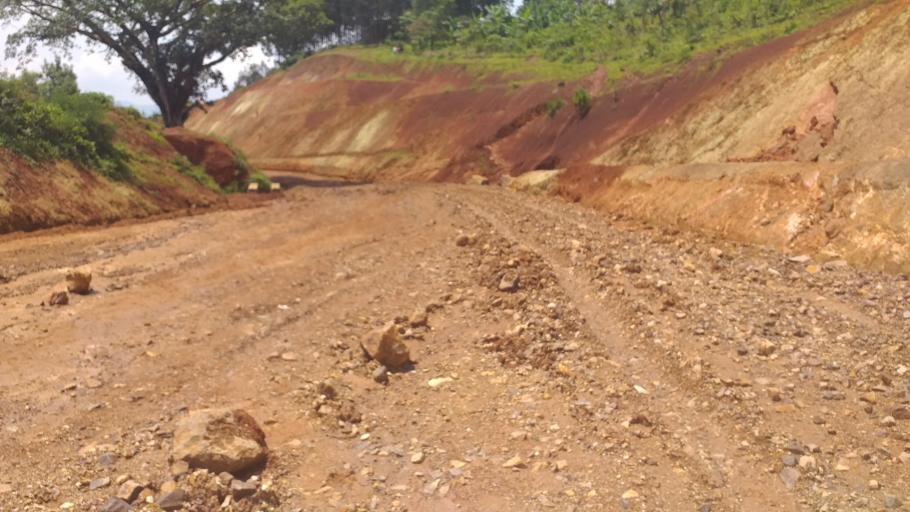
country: ET
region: Southern Nations, Nationalities, and People's Region
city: Bako
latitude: 5.9811
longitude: 36.5269
